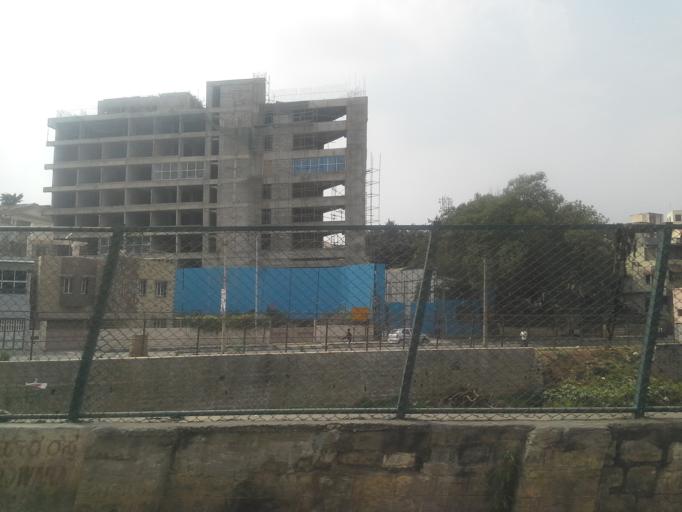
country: IN
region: Karnataka
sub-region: Bangalore Urban
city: Bangalore
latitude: 12.9763
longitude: 77.6202
